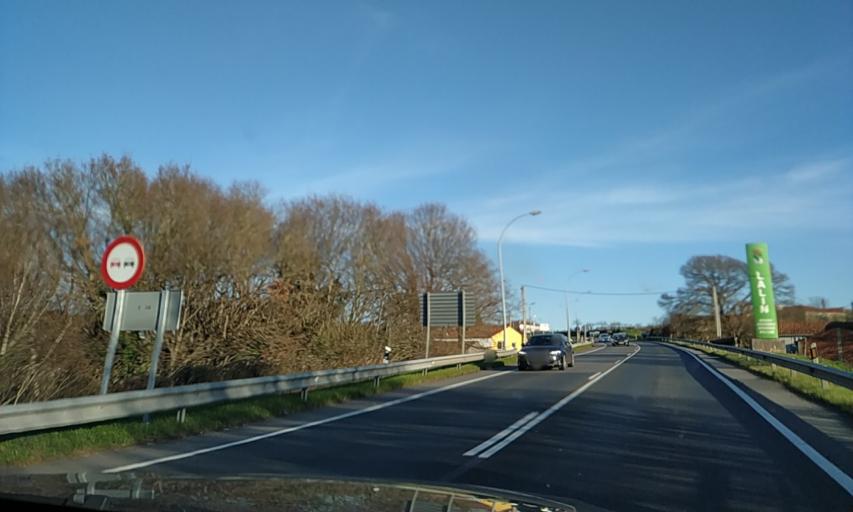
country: ES
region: Galicia
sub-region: Provincia de Pontevedra
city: Silleda
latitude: 42.6841
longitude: -8.1979
